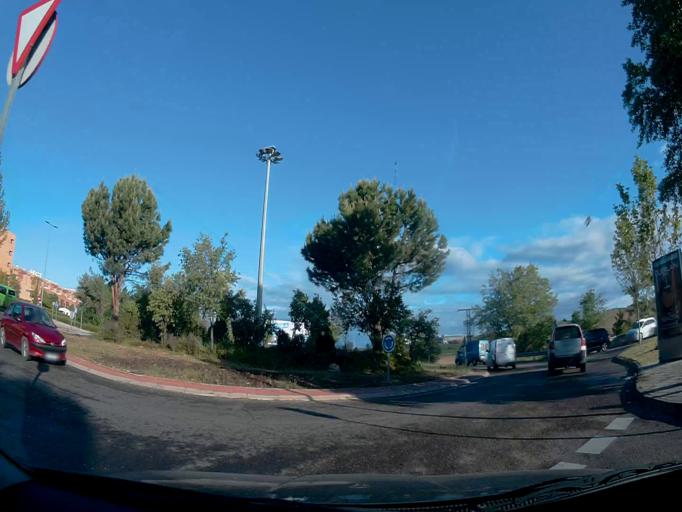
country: ES
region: Madrid
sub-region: Provincia de Madrid
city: San Sebastian de los Reyes
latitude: 40.5632
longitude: -3.6171
